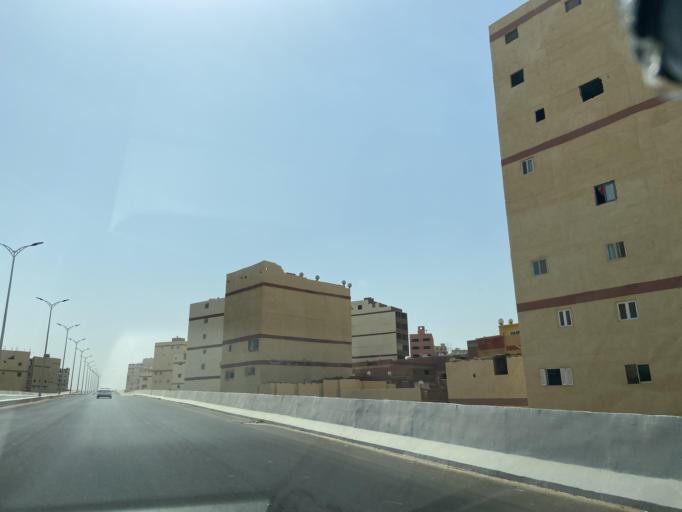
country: EG
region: Muhafazat al Qahirah
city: Cairo
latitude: 30.0666
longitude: 31.3836
